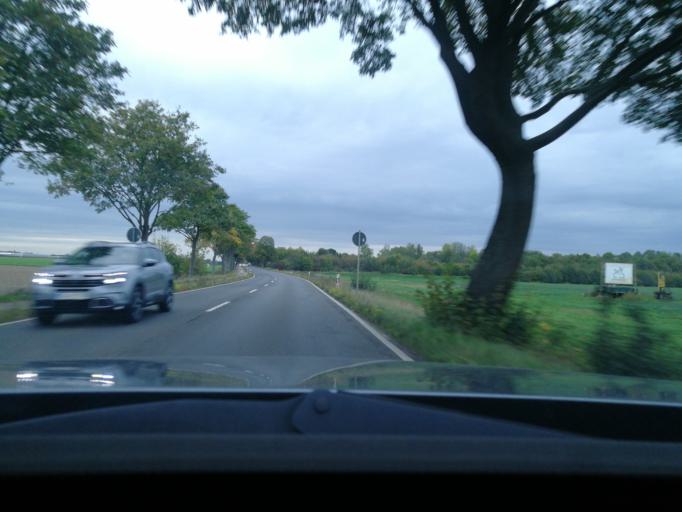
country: DE
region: North Rhine-Westphalia
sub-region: Regierungsbezirk Dusseldorf
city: Dormagen
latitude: 51.1219
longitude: 6.7655
